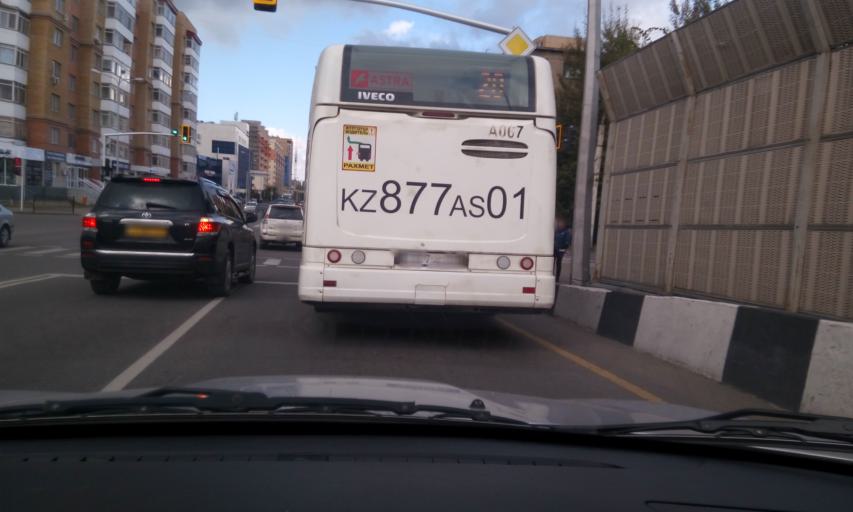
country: KZ
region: Astana Qalasy
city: Astana
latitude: 51.1598
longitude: 71.4627
